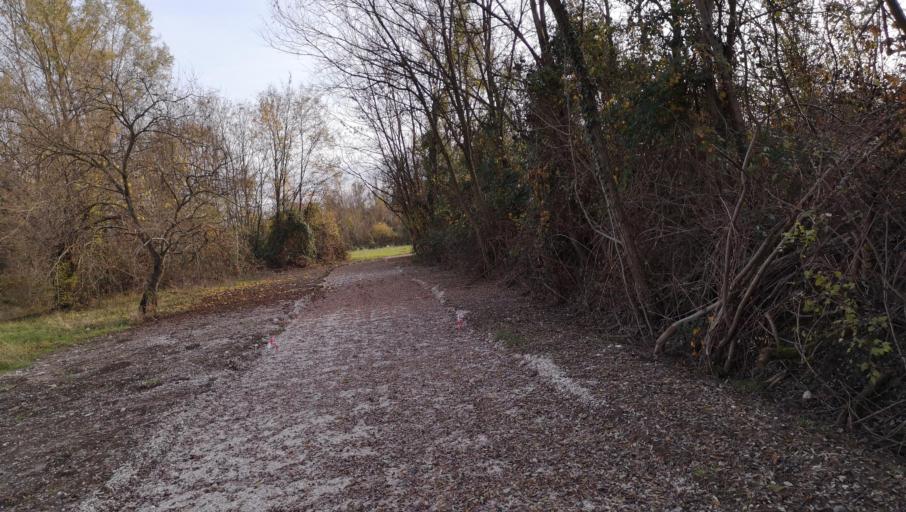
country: IT
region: Friuli Venezia Giulia
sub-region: Provincia di Udine
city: Magnano in Riviera
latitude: 46.2151
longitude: 13.1934
